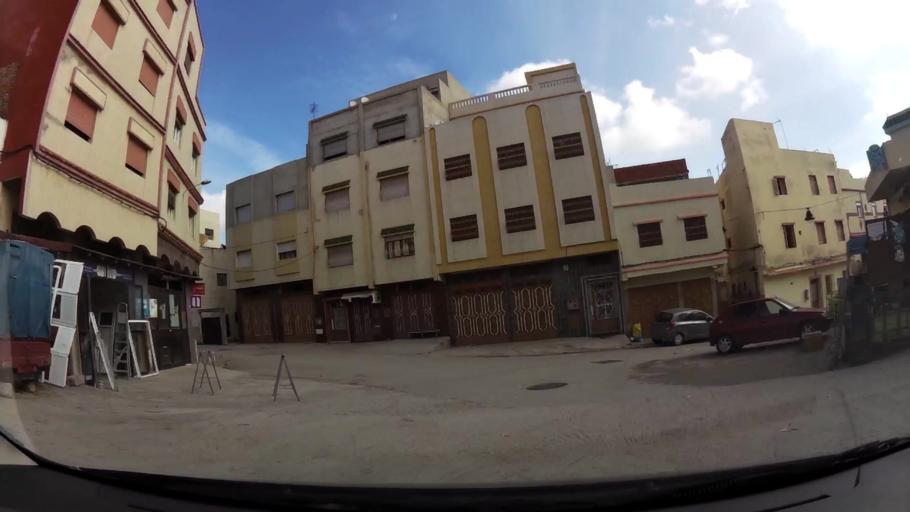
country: MA
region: Tanger-Tetouan
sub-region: Tanger-Assilah
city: Tangier
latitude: 35.7705
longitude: -5.7719
